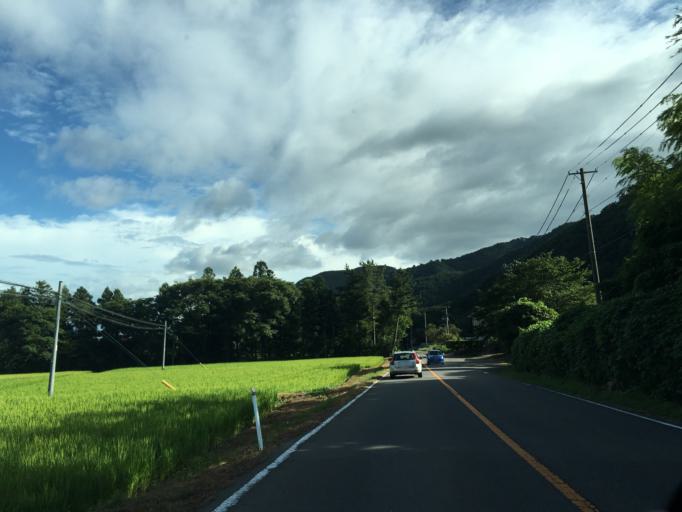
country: JP
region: Fukushima
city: Motomiya
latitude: 37.5164
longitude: 140.2703
